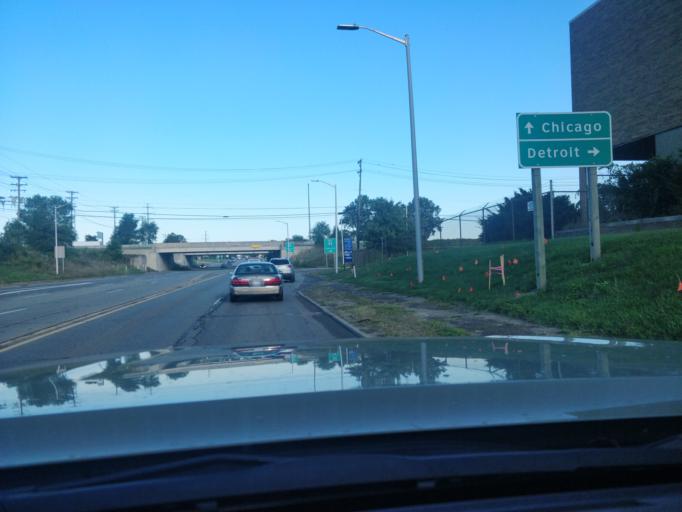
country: US
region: Michigan
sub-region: Wayne County
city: Melvindale
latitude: 42.2844
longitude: -83.1945
